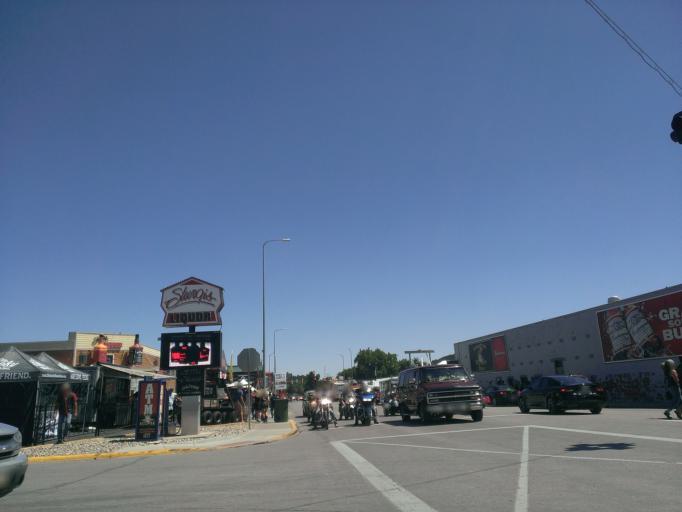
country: US
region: South Dakota
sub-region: Meade County
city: Sturgis
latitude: 44.4156
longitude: -103.5116
